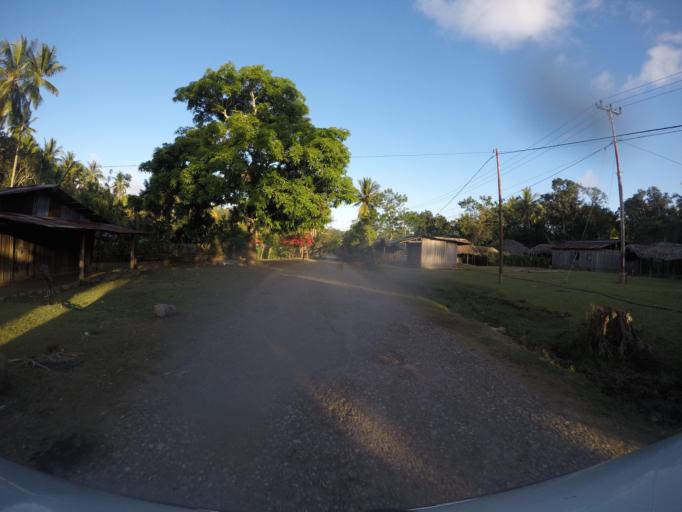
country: TL
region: Baucau
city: Venilale
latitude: -8.7333
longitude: 126.7117
